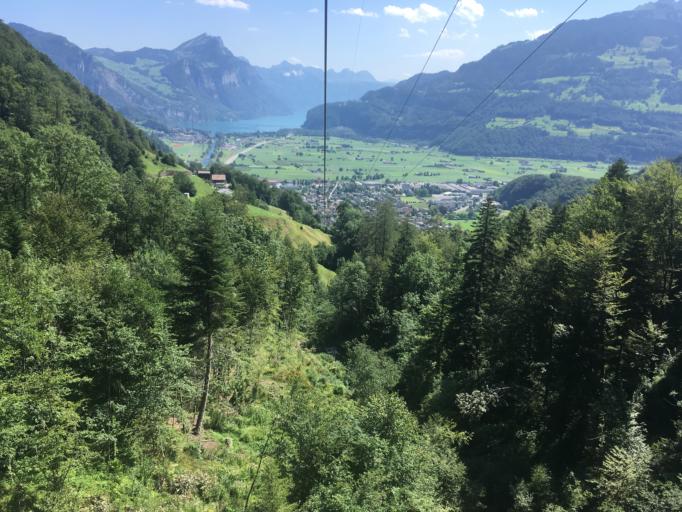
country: CH
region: Glarus
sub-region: Glarus
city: Niederurnen
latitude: 47.1253
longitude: 9.0319
